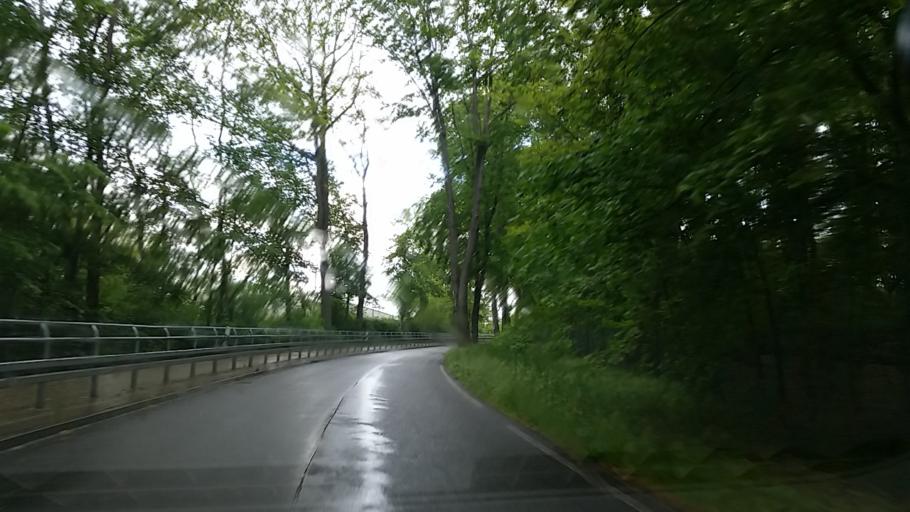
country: DE
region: Brandenburg
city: Diensdorf-Radlow
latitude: 52.2490
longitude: 14.0331
